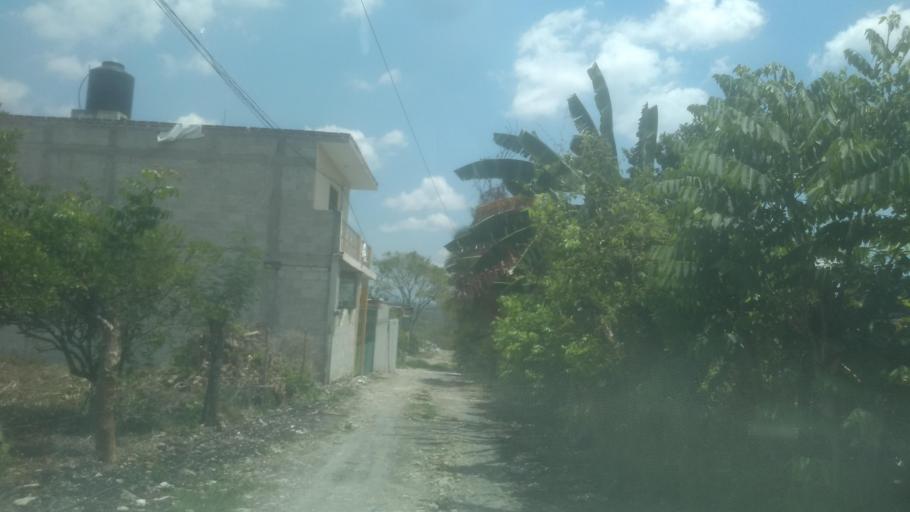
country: MX
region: Veracruz
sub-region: Emiliano Zapata
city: Plan del Rio
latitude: 19.3932
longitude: -96.6360
